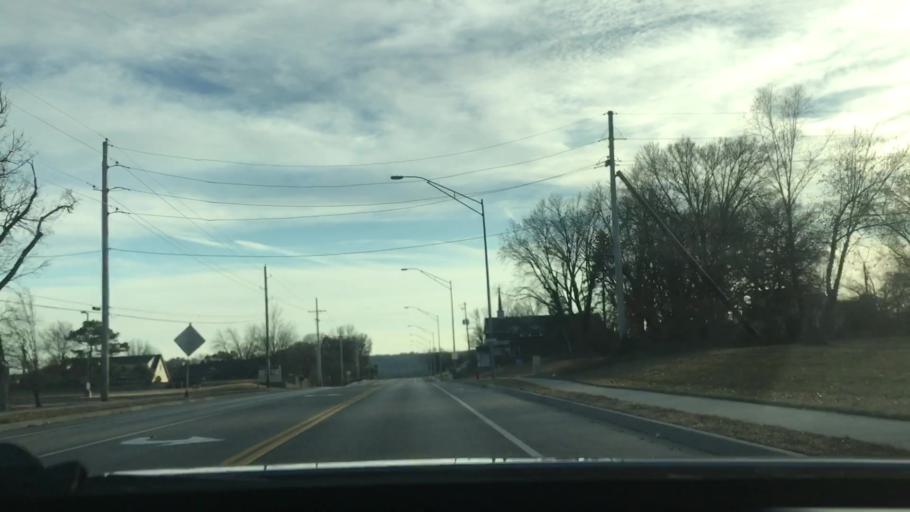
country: US
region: Missouri
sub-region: Jackson County
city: Independence
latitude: 39.0315
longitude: -94.3881
